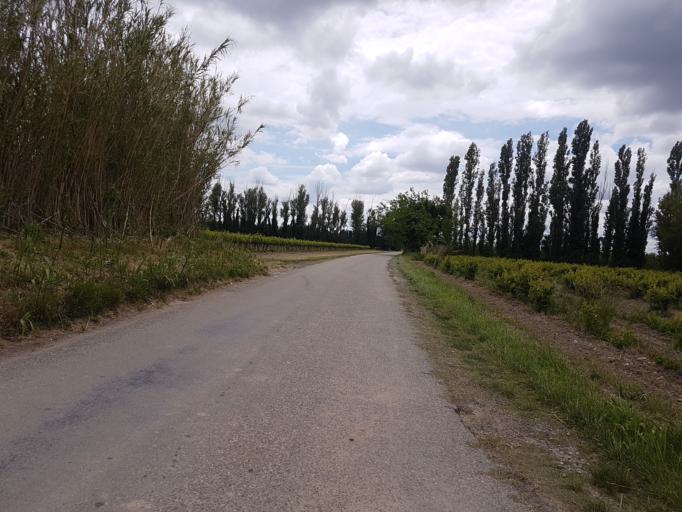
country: FR
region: Languedoc-Roussillon
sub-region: Departement du Gard
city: Vallabregues
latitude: 43.8794
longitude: 4.6282
